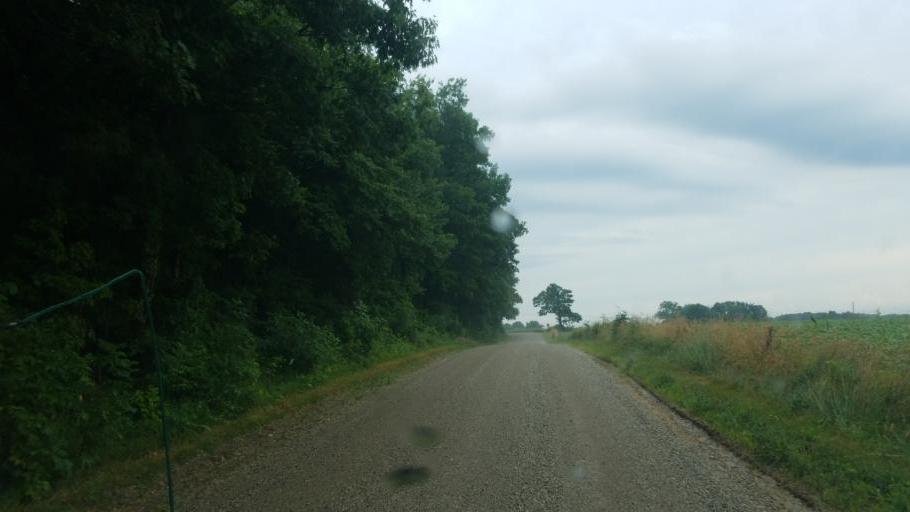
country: US
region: Indiana
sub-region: Steuben County
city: Hamilton
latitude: 41.5163
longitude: -84.9328
